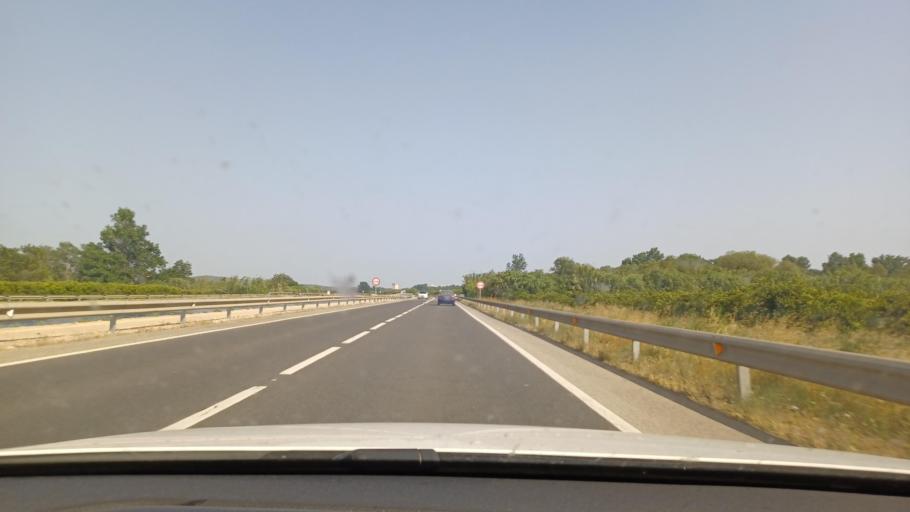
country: ES
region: Catalonia
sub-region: Provincia de Tarragona
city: Masdenverge
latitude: 40.7532
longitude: 0.5428
